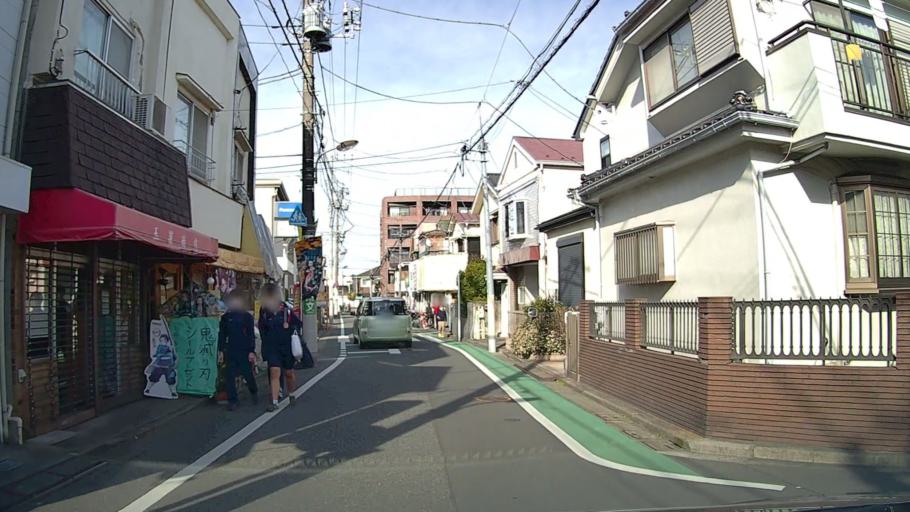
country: JP
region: Saitama
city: Wako
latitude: 35.7515
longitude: 139.6149
